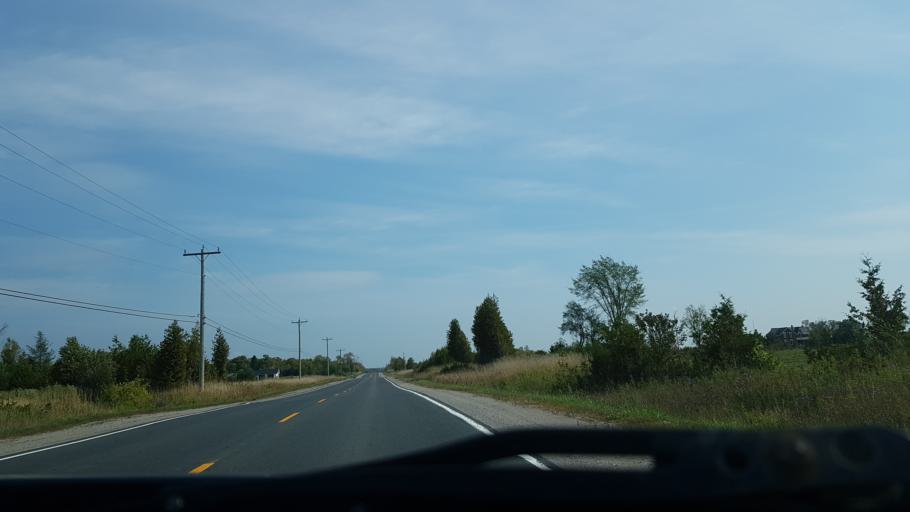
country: CA
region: Ontario
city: Orillia
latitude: 44.6427
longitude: -79.1565
